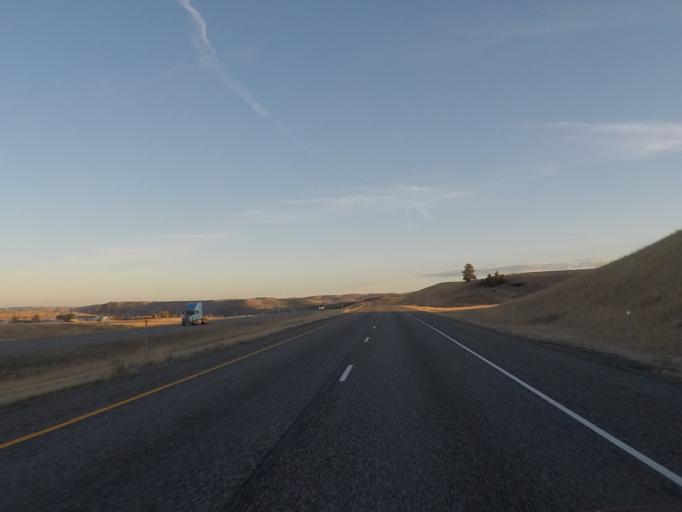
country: US
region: Montana
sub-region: Sweet Grass County
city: Big Timber
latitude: 45.7535
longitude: -109.7801
